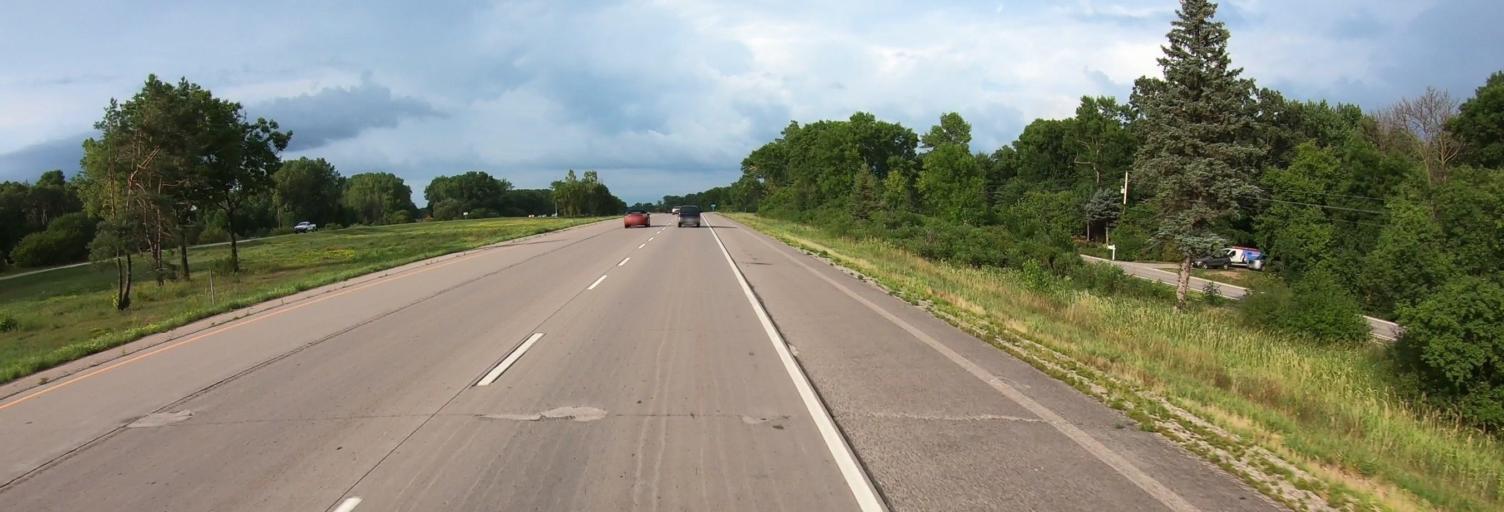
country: US
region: Minnesota
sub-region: Anoka County
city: Centerville
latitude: 45.1298
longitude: -93.0454
